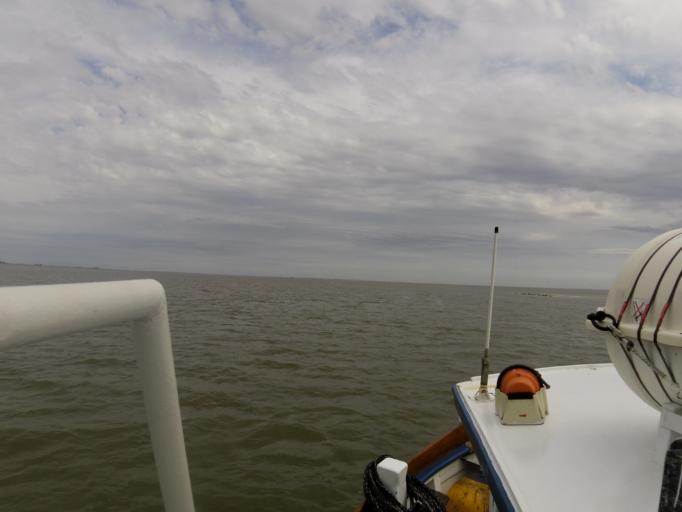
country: DE
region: Schleswig-Holstein
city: Langeness
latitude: 54.6101
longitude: 8.5785
